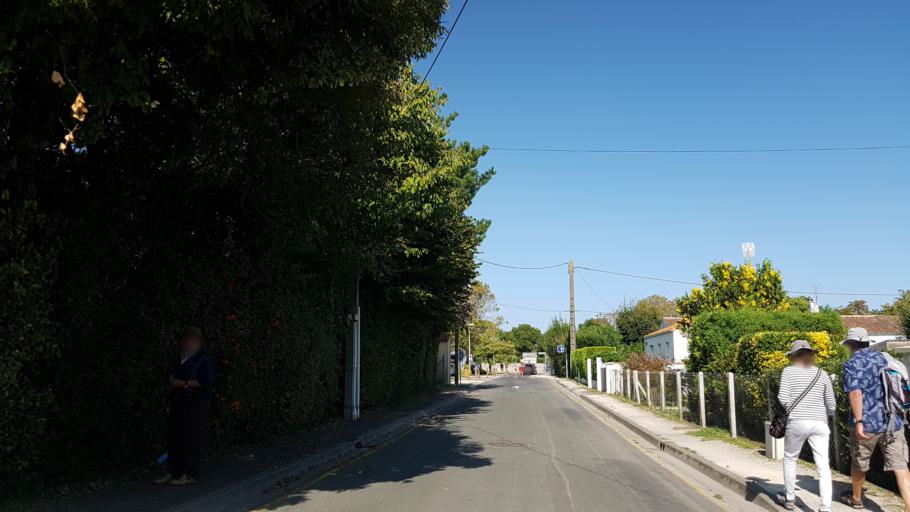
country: FR
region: Poitou-Charentes
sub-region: Departement de la Charente-Maritime
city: Breuillet
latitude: 45.7072
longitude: -1.0290
